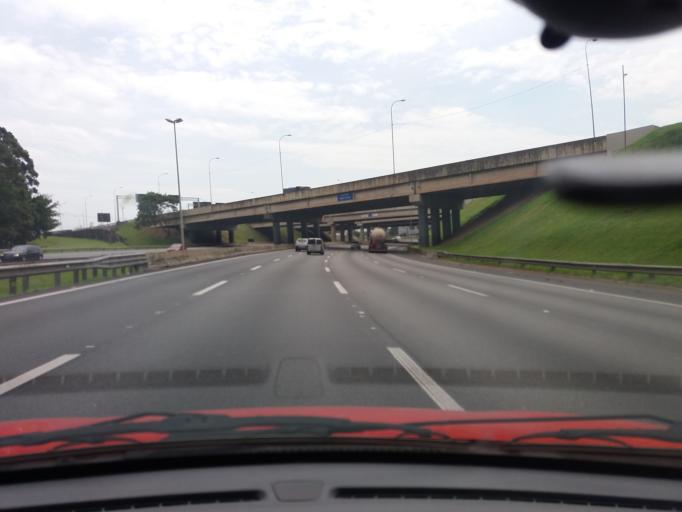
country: BR
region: Sao Paulo
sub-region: Carapicuiba
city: Carapicuiba
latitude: -23.5103
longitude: -46.8206
